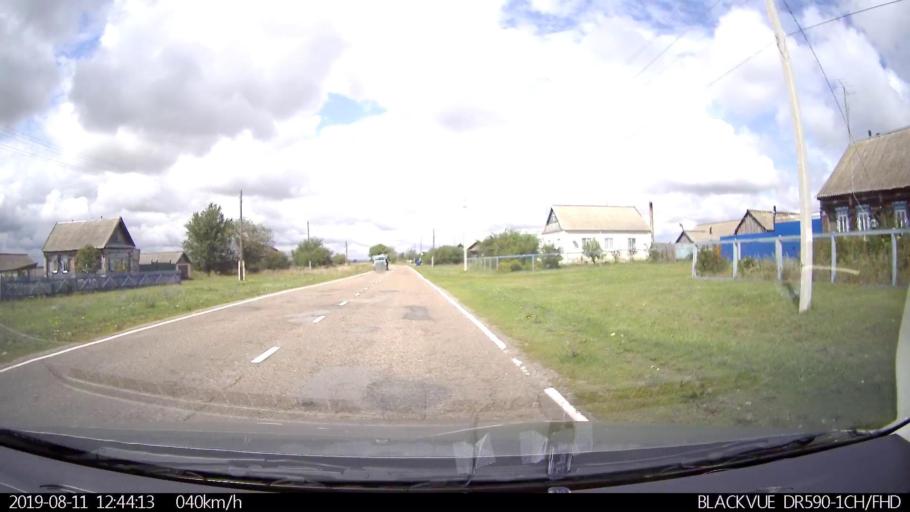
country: RU
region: Ulyanovsk
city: Ignatovka
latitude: 53.8538
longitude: 47.7378
